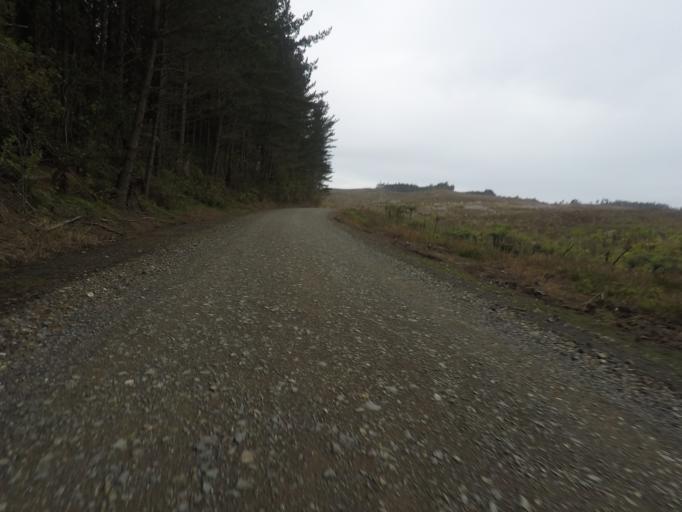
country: NZ
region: Auckland
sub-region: Auckland
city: Muriwai Beach
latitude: -36.7462
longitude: 174.5761
